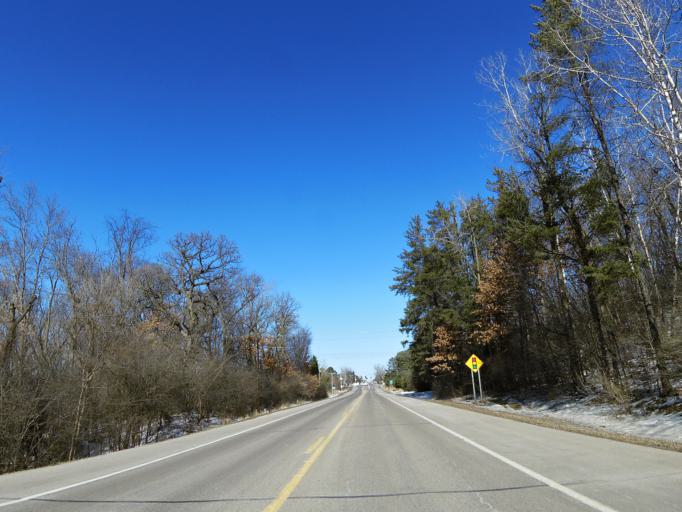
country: US
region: Minnesota
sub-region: Washington County
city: Lake Elmo
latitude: 45.0325
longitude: -92.8834
